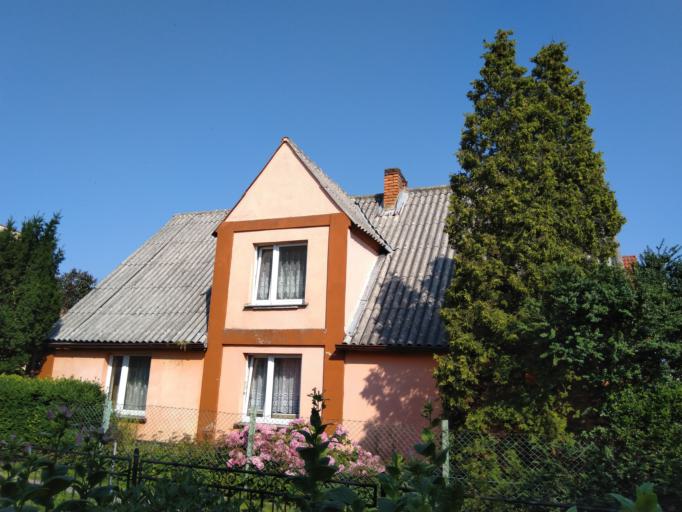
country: PL
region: Pomeranian Voivodeship
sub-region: Powiat pucki
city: Jastarnia
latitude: 54.7016
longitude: 18.6744
